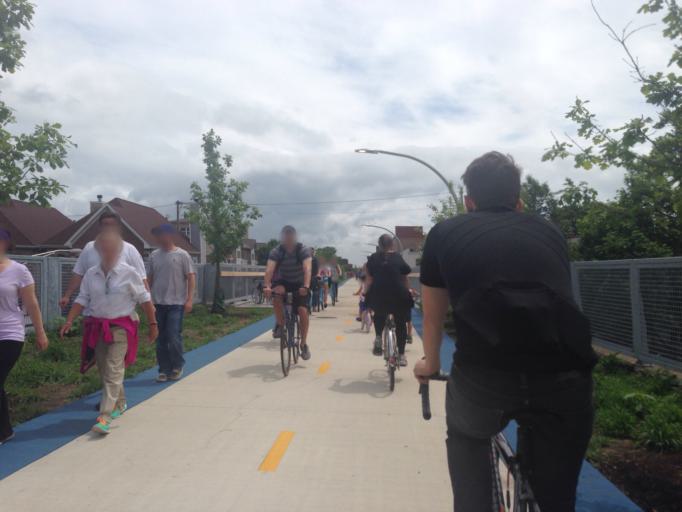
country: US
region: Illinois
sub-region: Cook County
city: Chicago
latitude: 41.9139
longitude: -87.6938
